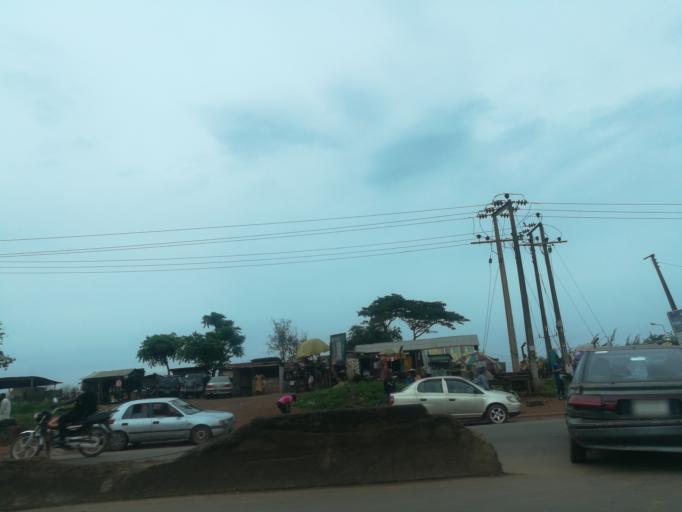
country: NG
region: Oyo
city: Ibadan
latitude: 7.3944
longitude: 3.9654
